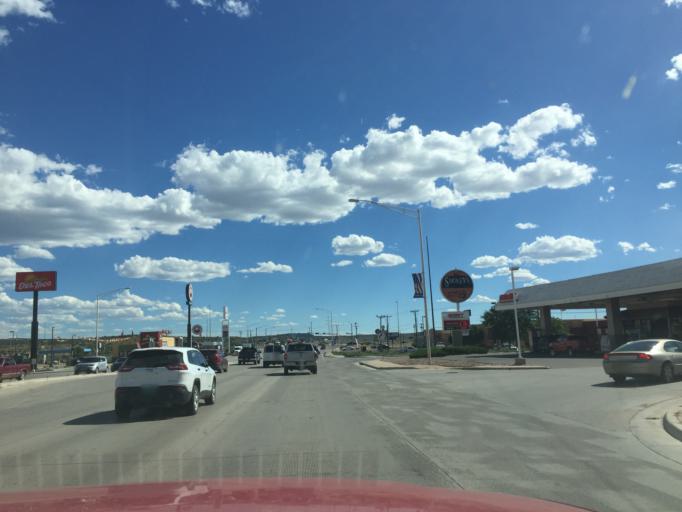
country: US
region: New Mexico
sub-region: McKinley County
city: Gallup
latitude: 35.5331
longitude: -108.7592
